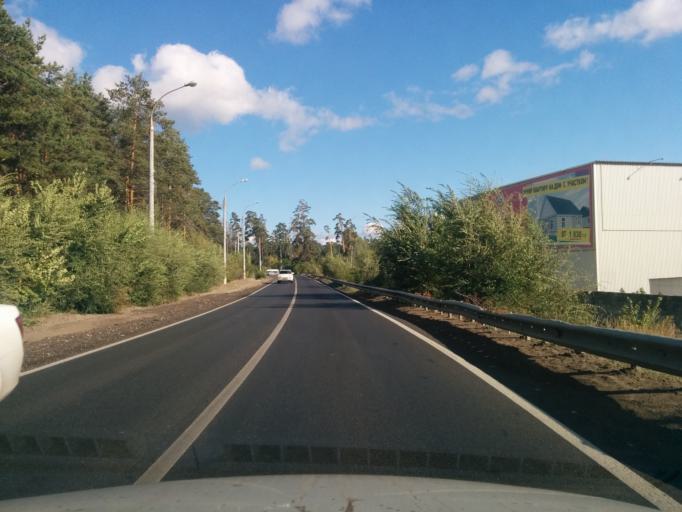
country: RU
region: Samara
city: Tol'yatti
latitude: 53.4772
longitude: 49.3239
